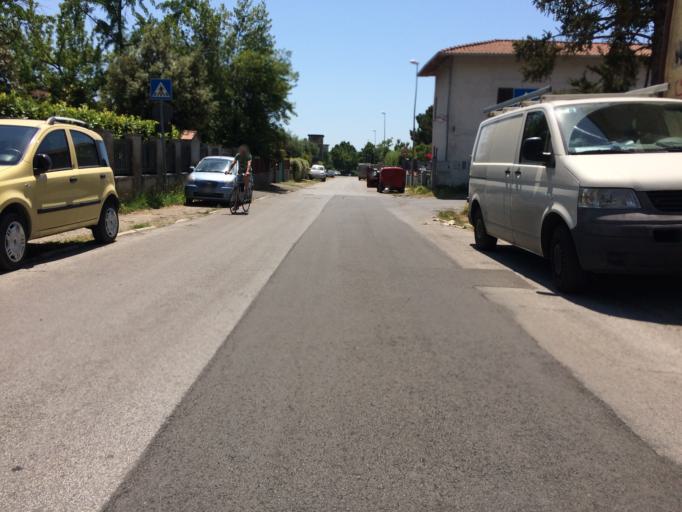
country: IT
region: Tuscany
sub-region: Provincia di Massa-Carrara
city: Massa
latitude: 44.0376
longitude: 10.1267
